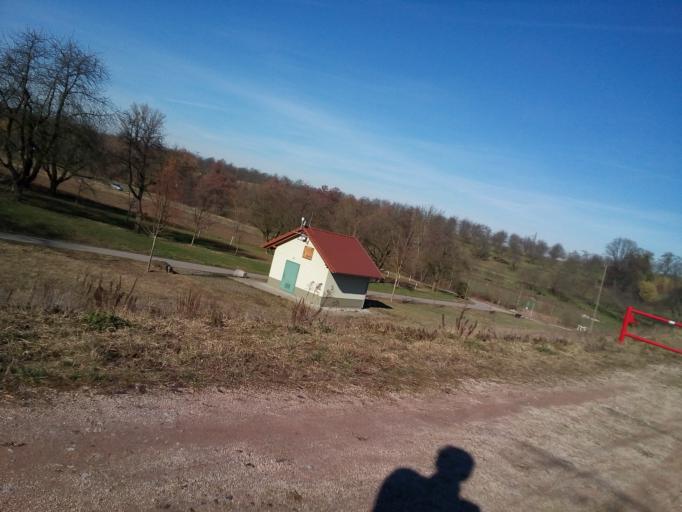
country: DE
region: Baden-Wuerttemberg
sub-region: Freiburg Region
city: Achern
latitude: 48.6104
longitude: 8.0640
